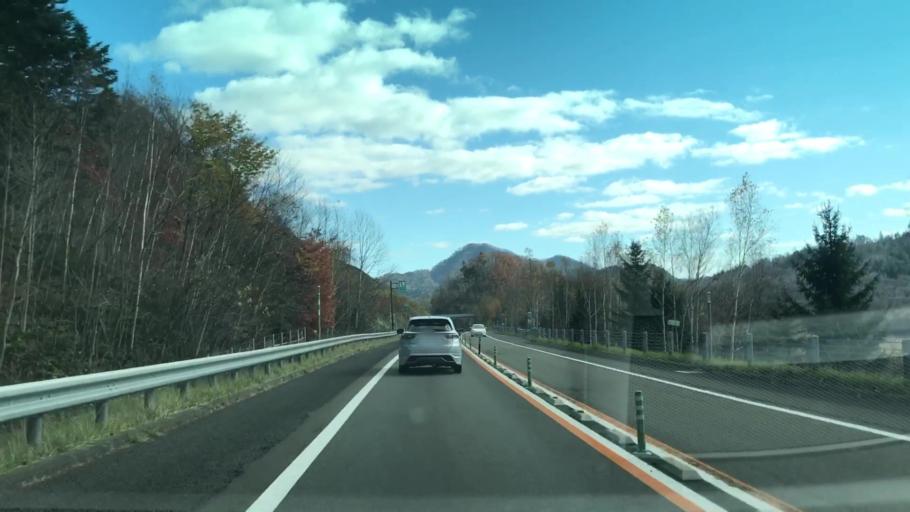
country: JP
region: Hokkaido
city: Chitose
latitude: 42.9116
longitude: 141.9782
